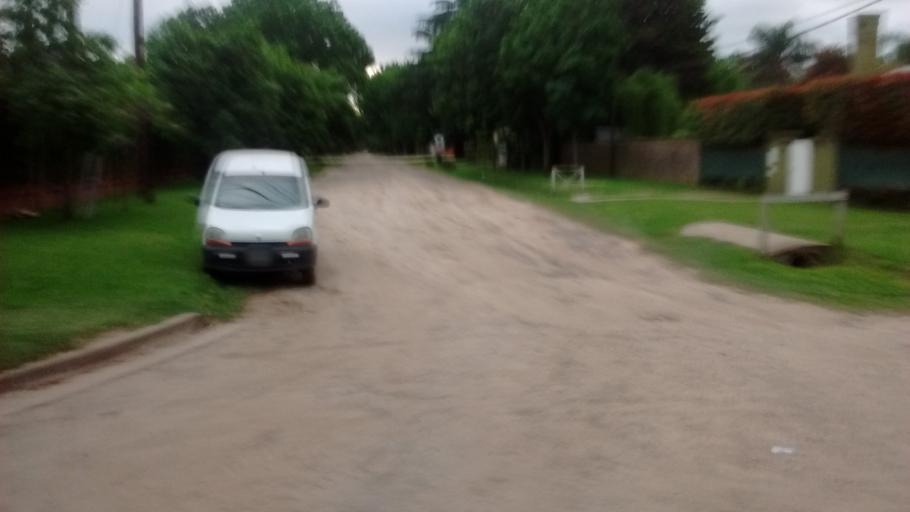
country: AR
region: Santa Fe
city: Funes
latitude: -32.9242
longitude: -60.8116
